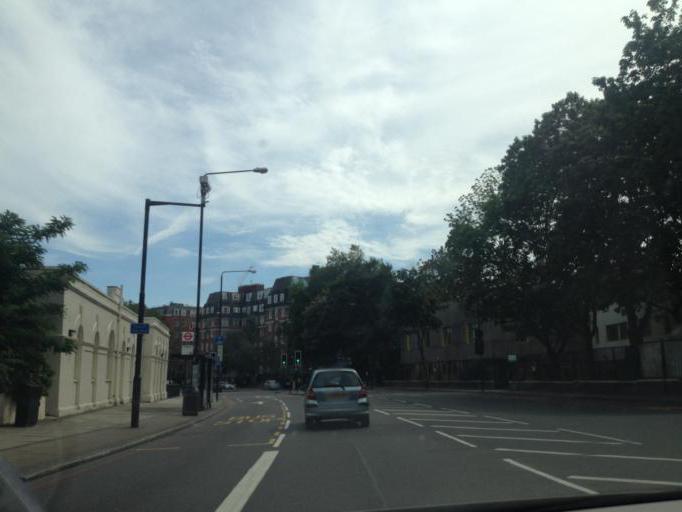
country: GB
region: England
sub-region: Greater London
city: Belsize Park
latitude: 51.5371
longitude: -0.1761
